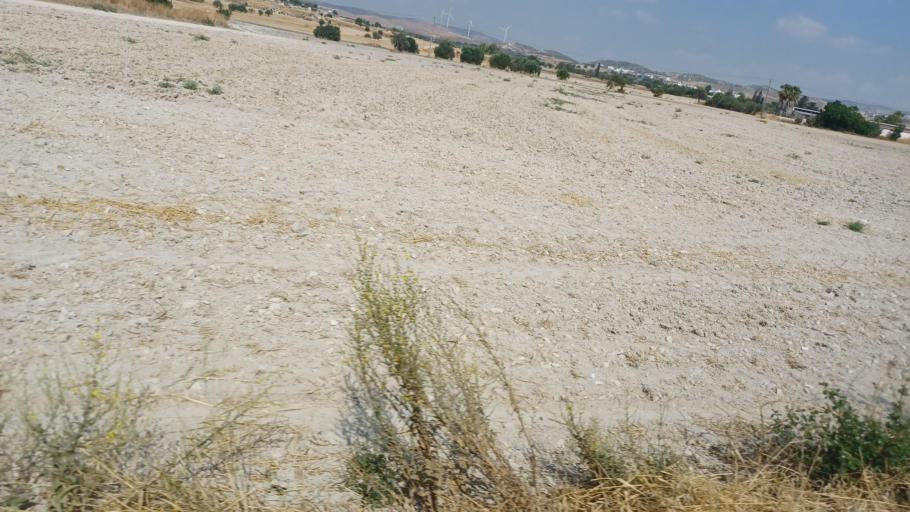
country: CY
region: Larnaka
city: Aradippou
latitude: 34.9214
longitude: 33.5379
